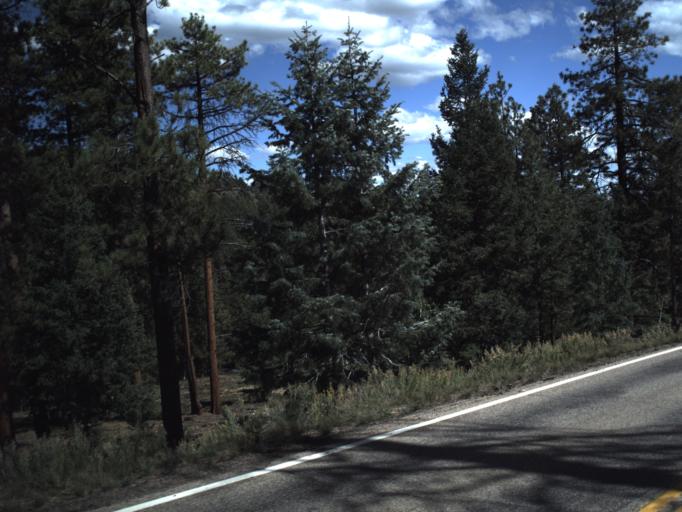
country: US
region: Utah
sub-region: Garfield County
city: Panguitch
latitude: 37.5129
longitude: -112.6345
